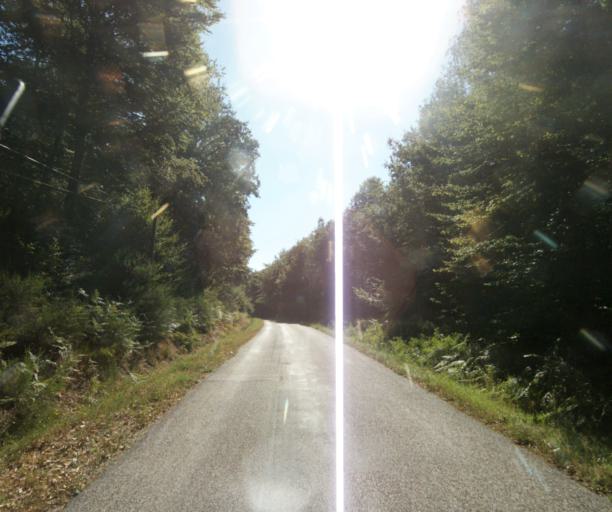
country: FR
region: Lorraine
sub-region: Departement des Vosges
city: Arches
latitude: 48.1446
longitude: 6.4852
